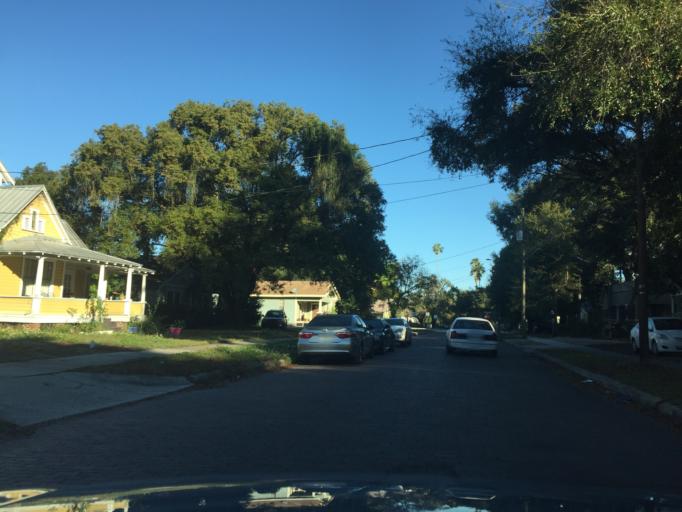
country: US
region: Florida
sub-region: Hillsborough County
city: Tampa
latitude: 27.9699
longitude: -82.4569
